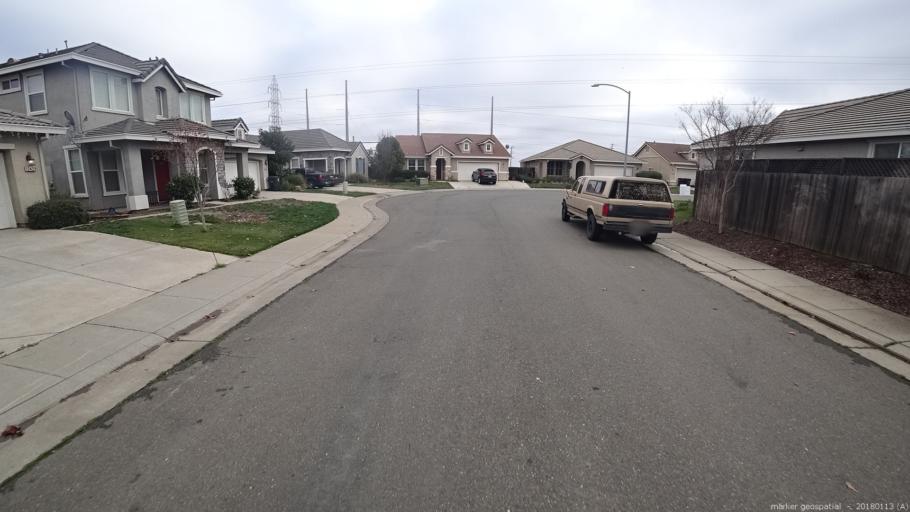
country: US
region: California
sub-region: Sacramento County
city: Gold River
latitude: 38.5539
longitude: -121.2104
